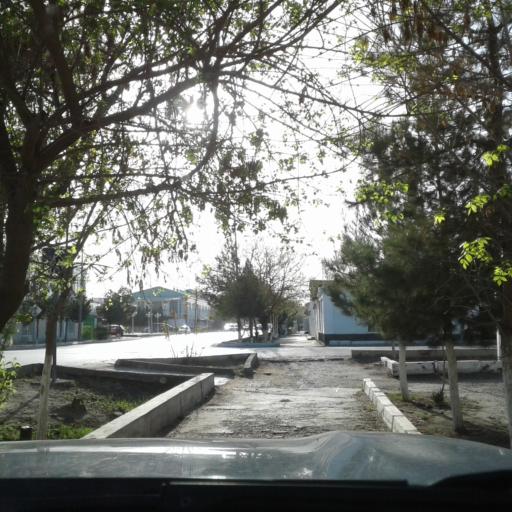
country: TM
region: Lebap
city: Turkmenabat
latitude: 39.0946
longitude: 63.5786
